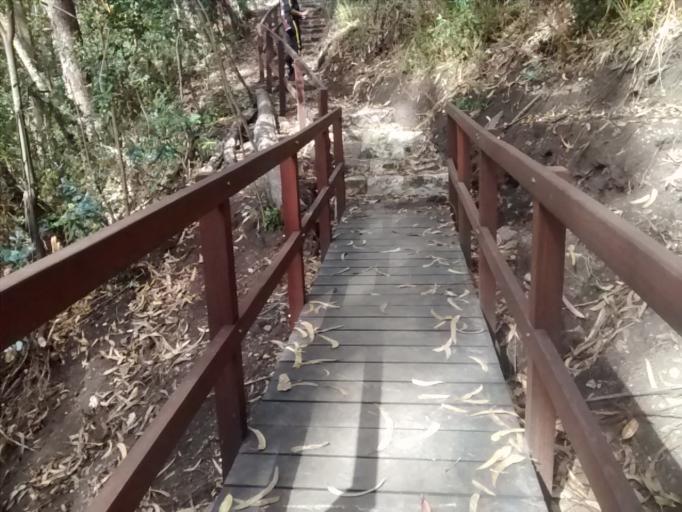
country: CO
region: Bogota D.C.
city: Bogota
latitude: 4.5974
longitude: -74.0590
